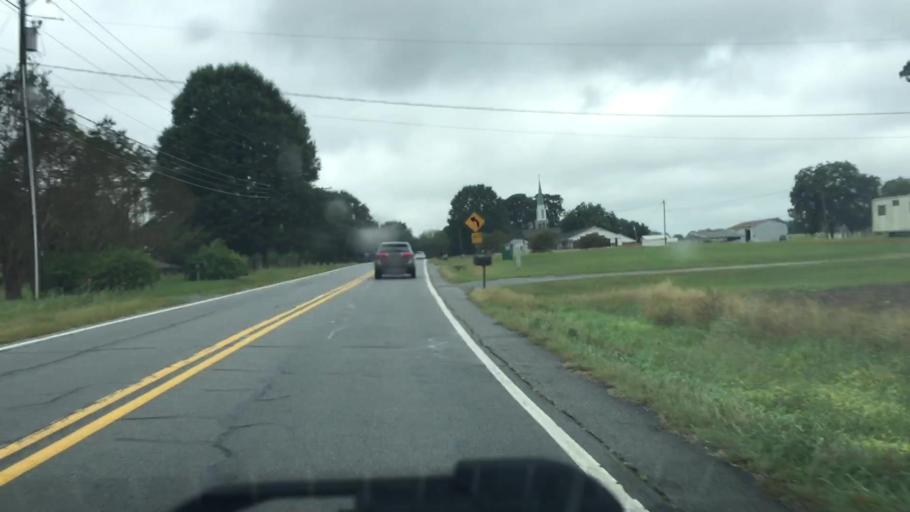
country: US
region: North Carolina
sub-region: Rowan County
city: China Grove
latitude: 35.6526
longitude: -80.5784
